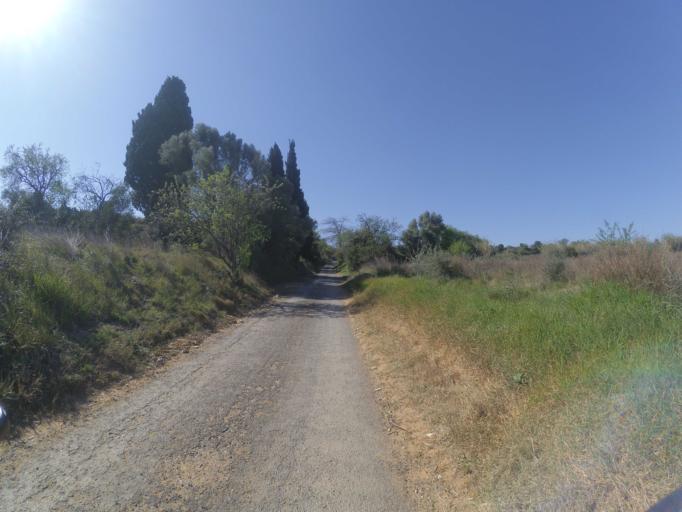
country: FR
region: Languedoc-Roussillon
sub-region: Departement des Pyrenees-Orientales
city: Baixas
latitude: 42.7419
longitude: 2.7986
